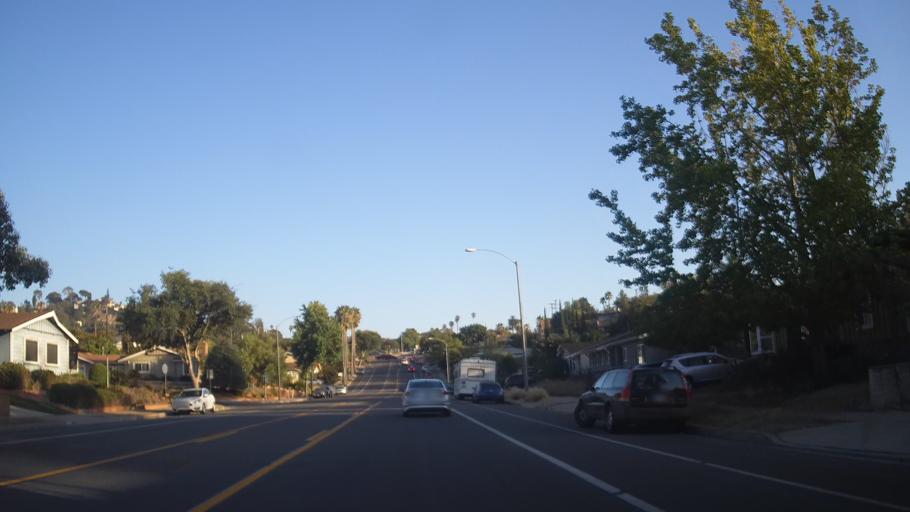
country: US
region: California
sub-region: San Diego County
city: La Mesa
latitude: 32.7830
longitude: -116.9977
